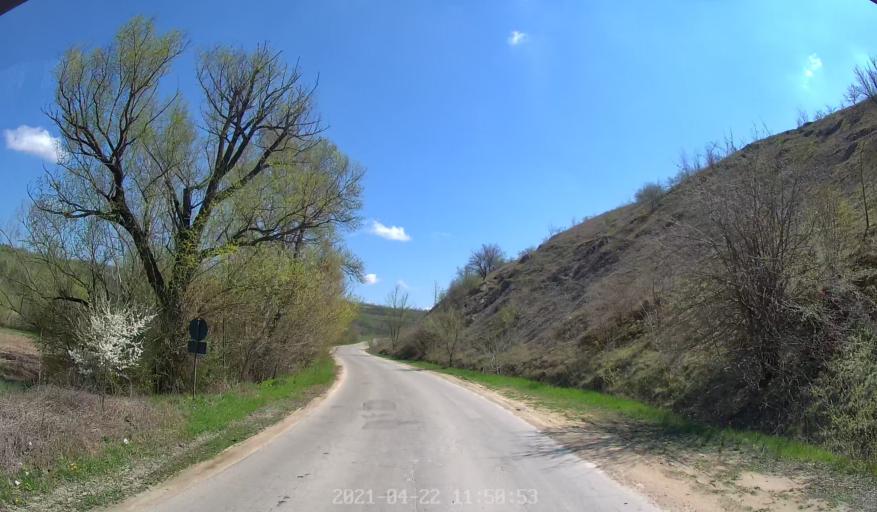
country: MD
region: Chisinau
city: Ciorescu
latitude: 47.1365
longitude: 28.9035
